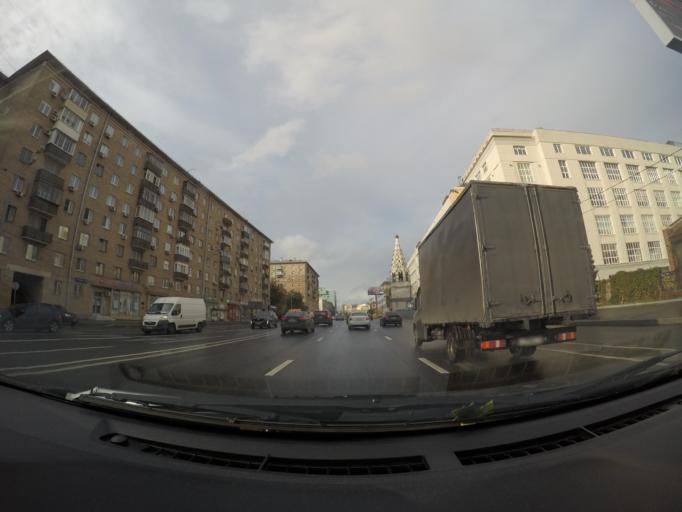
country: RU
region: Moscow
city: Mar'ina Roshcha
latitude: 55.8000
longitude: 37.5838
